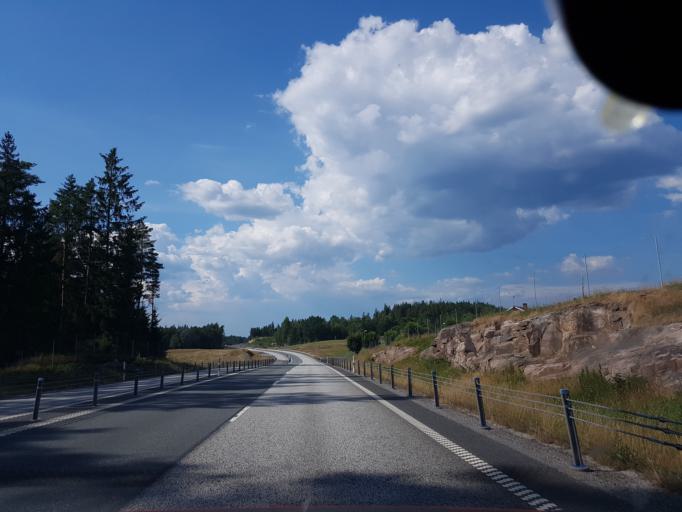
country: SE
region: Joenkoeping
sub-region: Gislaveds Kommun
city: Reftele
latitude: 57.2500
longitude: 13.6408
